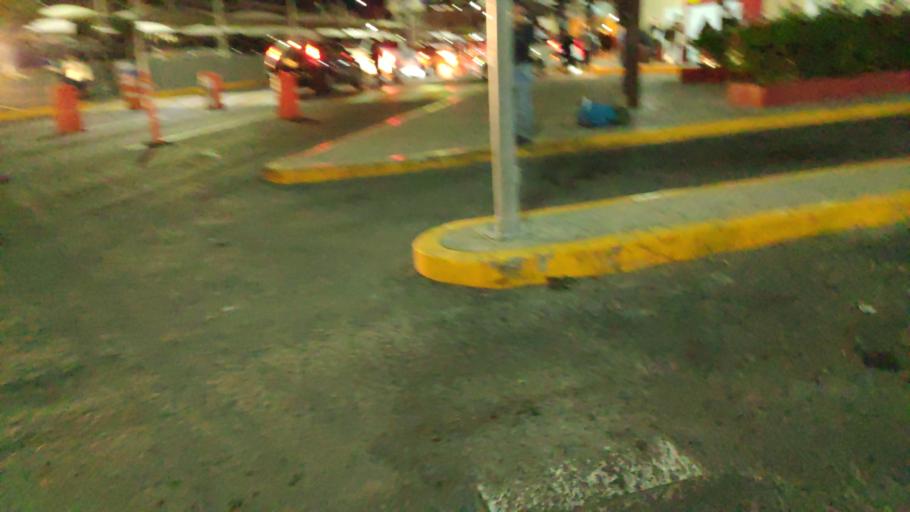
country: MX
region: Queretaro
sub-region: Queretaro
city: Santiago de Queretaro
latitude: 20.5785
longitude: -100.3595
